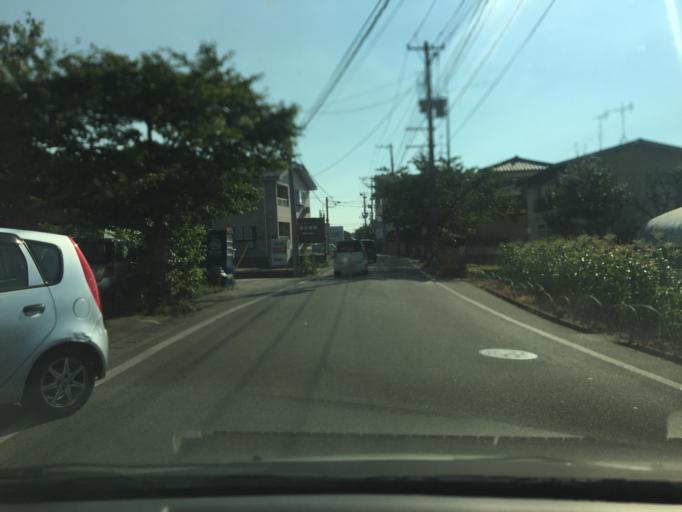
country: JP
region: Niigata
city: Niigata-shi
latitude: 37.8946
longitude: 139.0543
